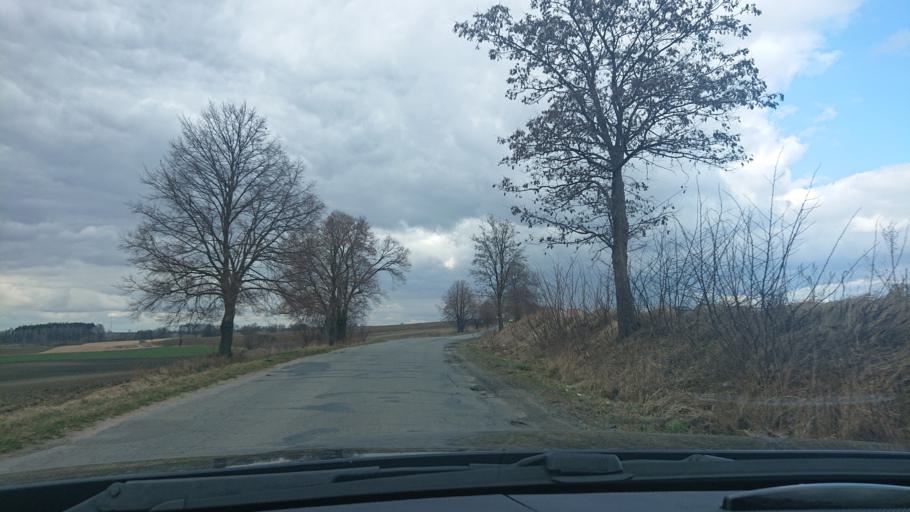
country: PL
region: Greater Poland Voivodeship
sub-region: Powiat gnieznienski
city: Niechanowo
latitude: 52.5563
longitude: 17.6968
